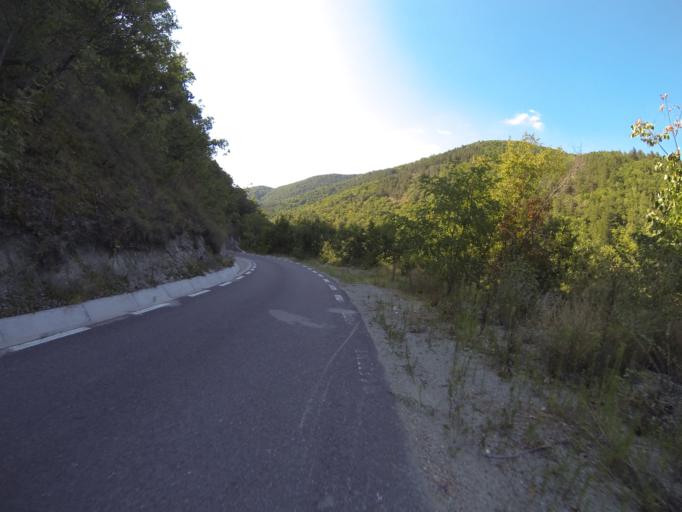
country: RO
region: Mehedinti
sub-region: Comuna Dubova
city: Dubova
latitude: 44.5430
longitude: 22.2104
